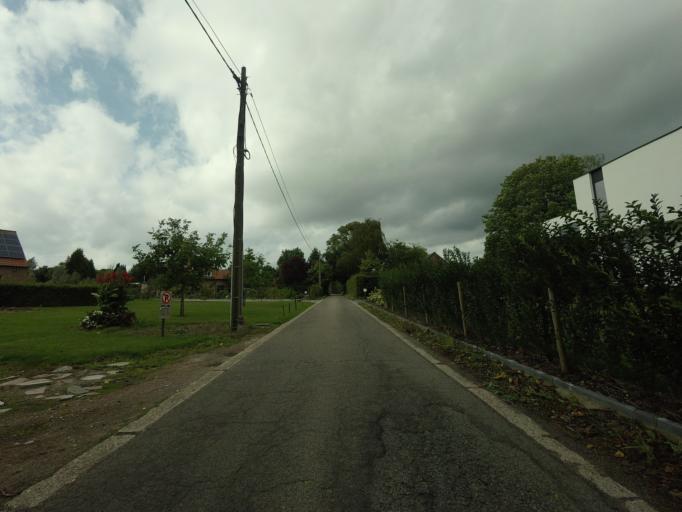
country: BE
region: Flanders
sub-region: Provincie Antwerpen
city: Aartselaar
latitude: 51.1075
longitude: 4.3974
